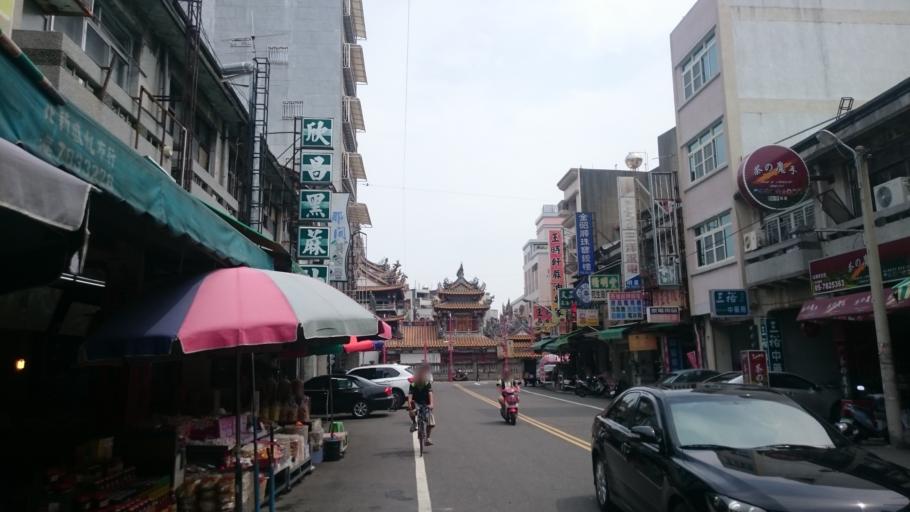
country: TW
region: Taiwan
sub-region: Chiayi
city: Taibao
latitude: 23.5681
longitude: 120.3038
